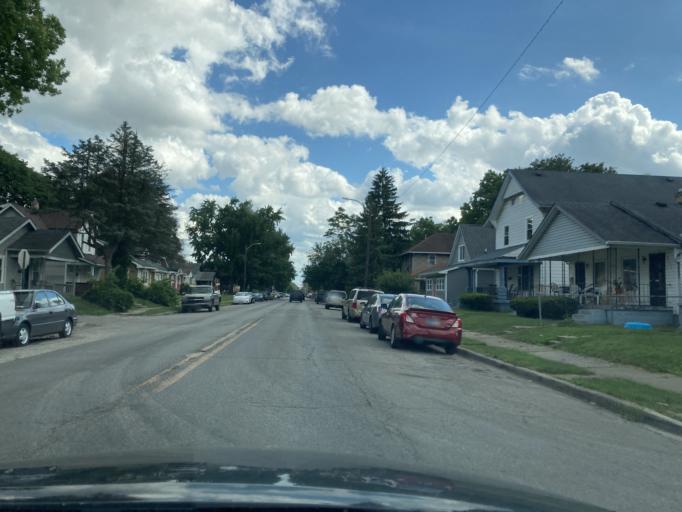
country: US
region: Indiana
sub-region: Marion County
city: Broad Ripple
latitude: 39.8307
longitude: -86.1640
